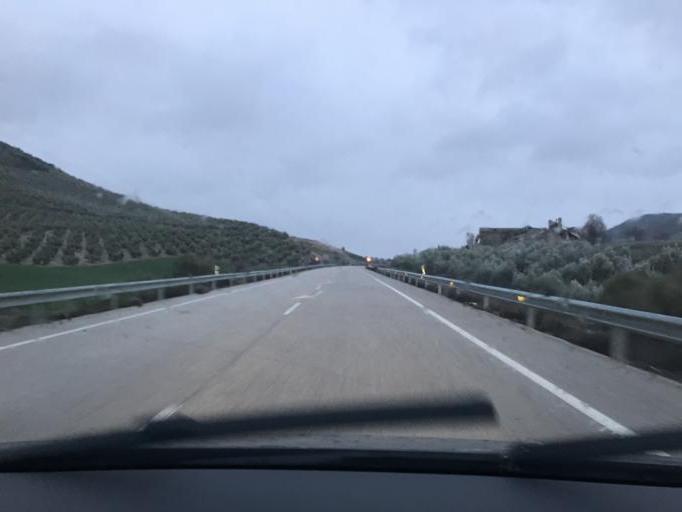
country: ES
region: Andalusia
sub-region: Provincia de Granada
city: Campotejar
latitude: 37.4560
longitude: -3.6145
